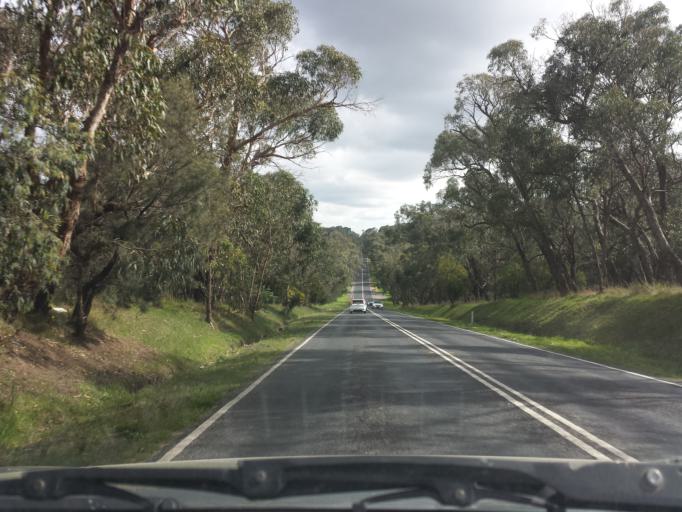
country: AU
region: Victoria
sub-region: Yarra Ranges
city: Lysterfield
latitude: -37.9395
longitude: 145.3163
